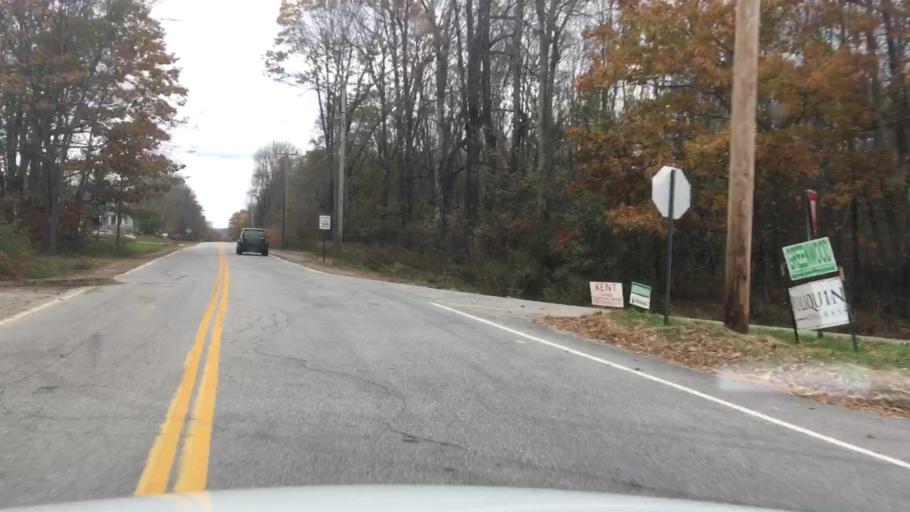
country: US
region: Maine
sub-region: Kennebec County
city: Monmouth
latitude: 44.1836
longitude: -70.0653
